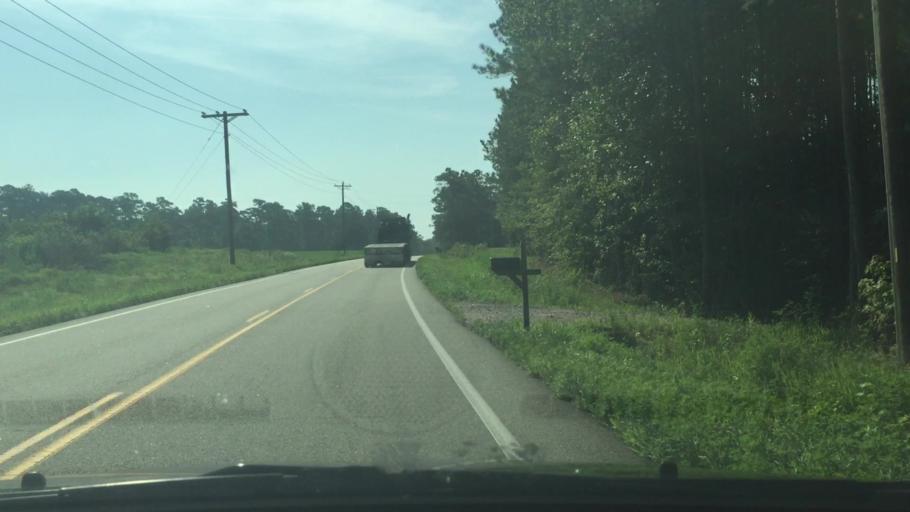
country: US
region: Virginia
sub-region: Sussex County
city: Sussex
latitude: 37.0519
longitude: -77.3198
